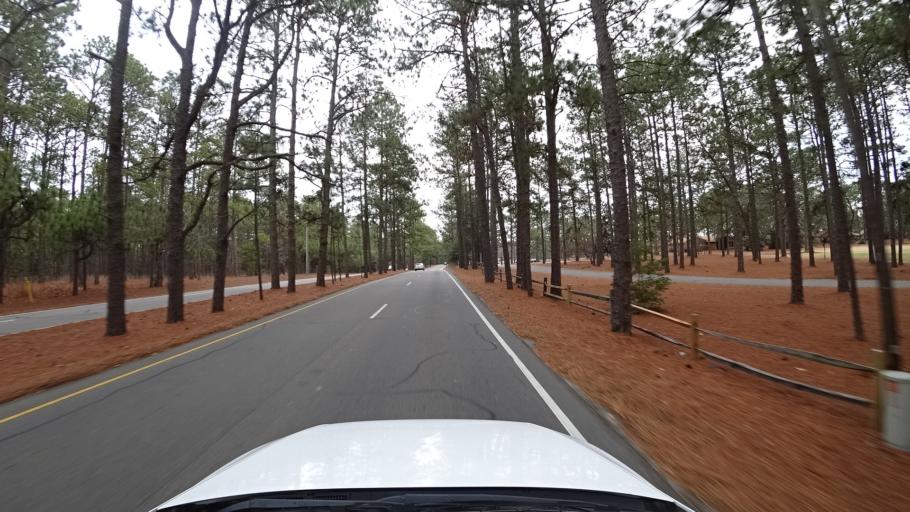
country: US
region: North Carolina
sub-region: Moore County
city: Southern Pines
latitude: 35.1981
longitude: -79.4096
